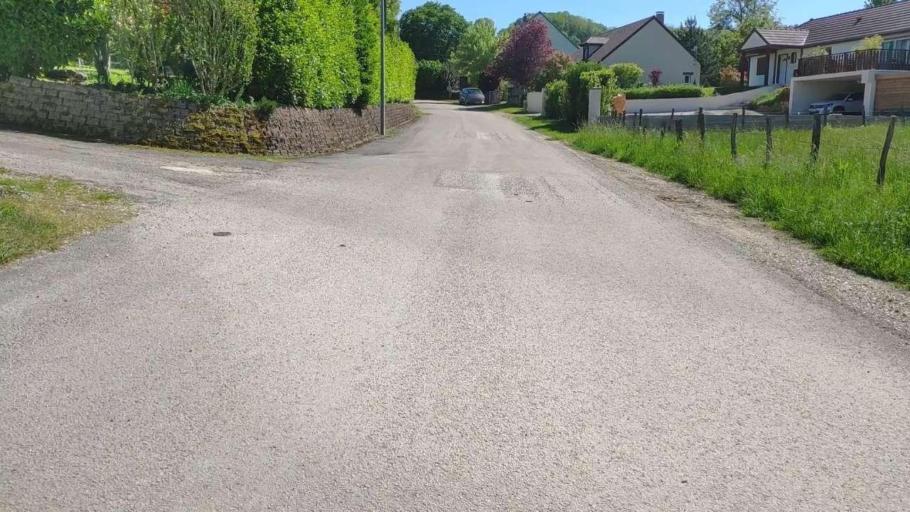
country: FR
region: Franche-Comte
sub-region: Departement du Jura
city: Perrigny
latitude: 46.7313
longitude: 5.5827
